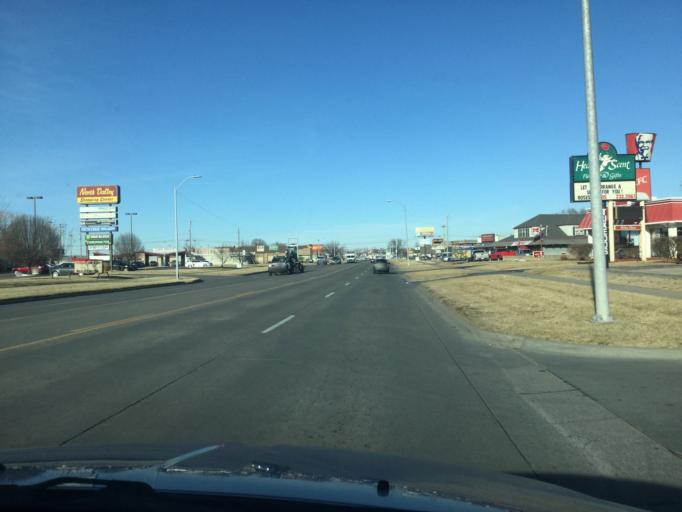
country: US
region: Kansas
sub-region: Shawnee County
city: Topeka
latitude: 39.0808
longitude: -95.6671
